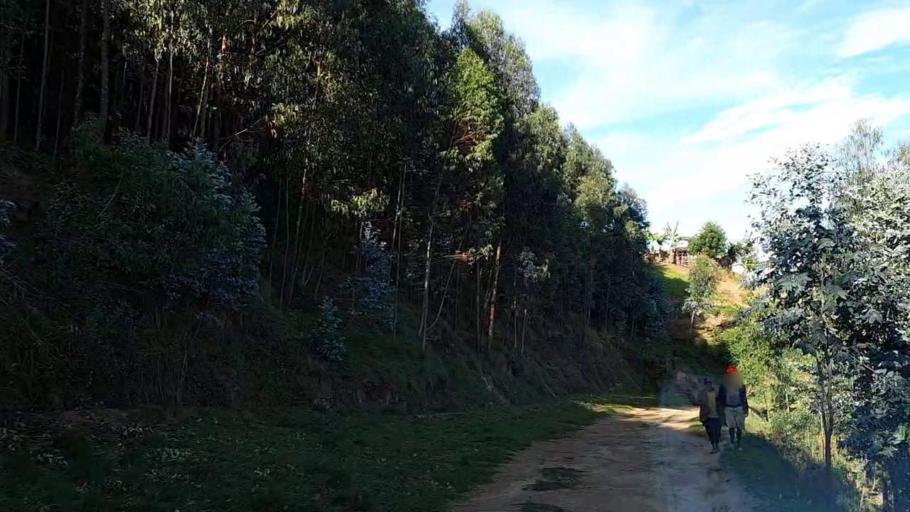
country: RW
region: Southern Province
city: Gikongoro
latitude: -2.4123
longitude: 29.5195
